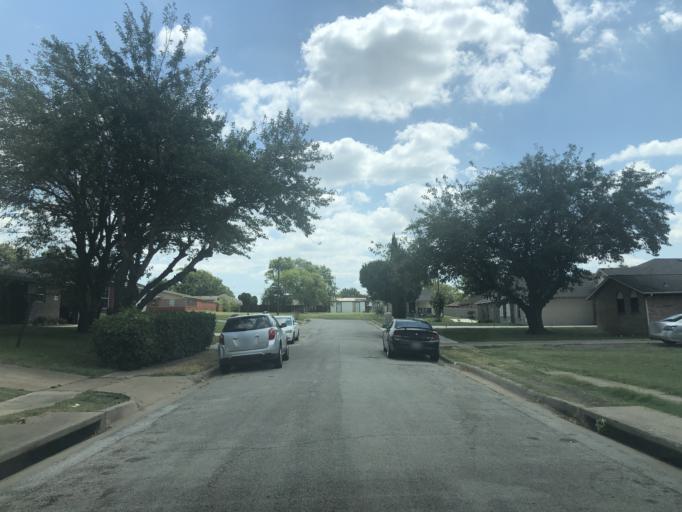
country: US
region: Texas
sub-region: Dallas County
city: Grand Prairie
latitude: 32.7361
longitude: -97.0284
